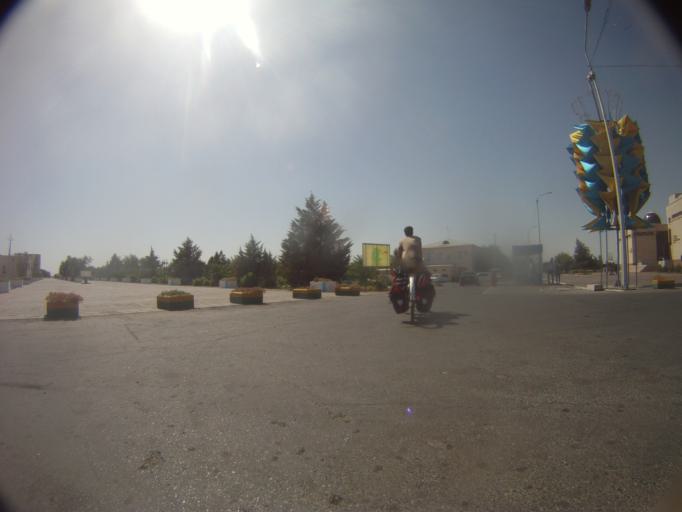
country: KZ
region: Ongtustik Qazaqstan
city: Turkestan
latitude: 43.2988
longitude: 68.2761
